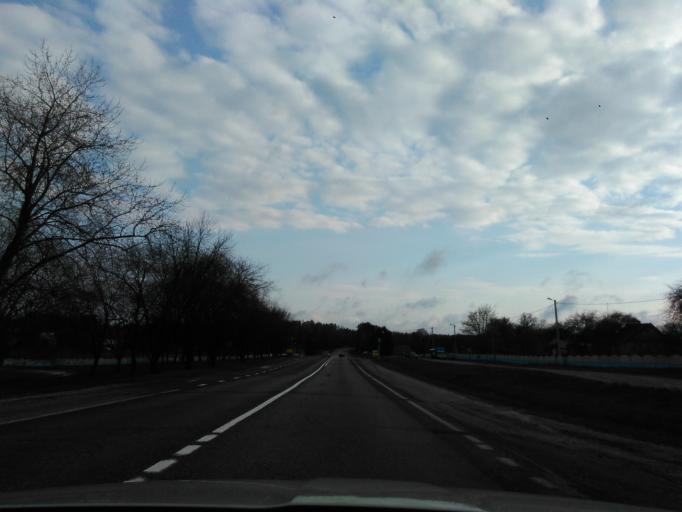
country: BY
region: Minsk
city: Lahoysk
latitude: 54.2923
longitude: 27.8729
